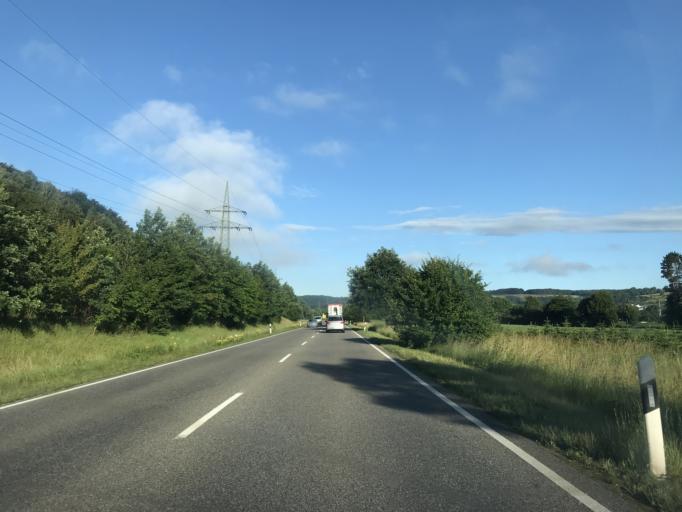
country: DE
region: Baden-Wuerttemberg
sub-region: Freiburg Region
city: Steinen
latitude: 47.6383
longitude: 7.7203
